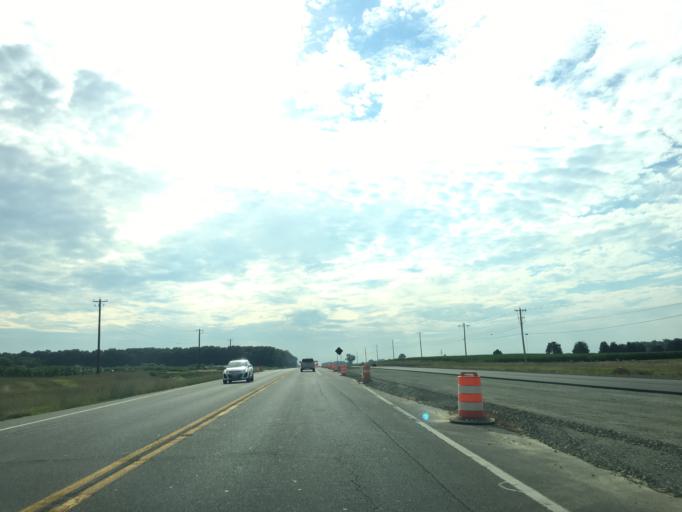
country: US
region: Maryland
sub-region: Caroline County
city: Ridgely
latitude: 38.9268
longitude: -75.9940
